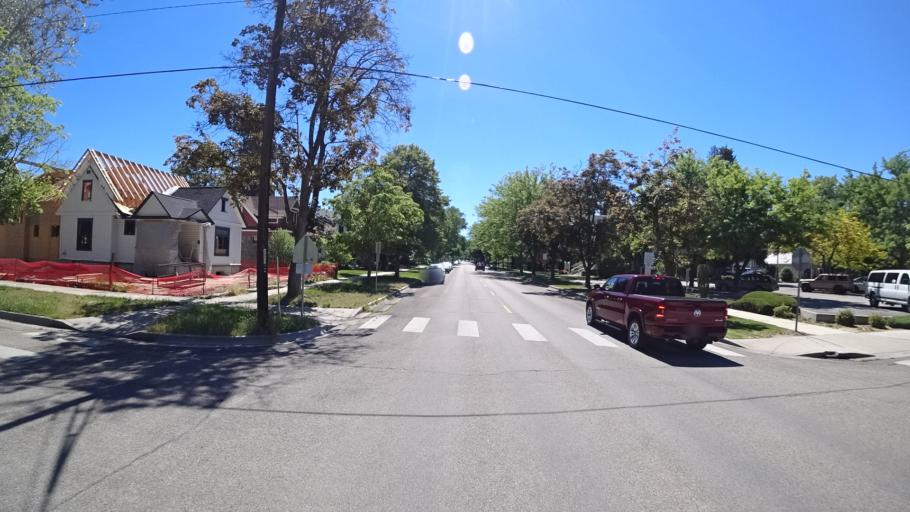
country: US
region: Idaho
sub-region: Ada County
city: Boise
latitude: 43.6227
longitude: -116.2018
